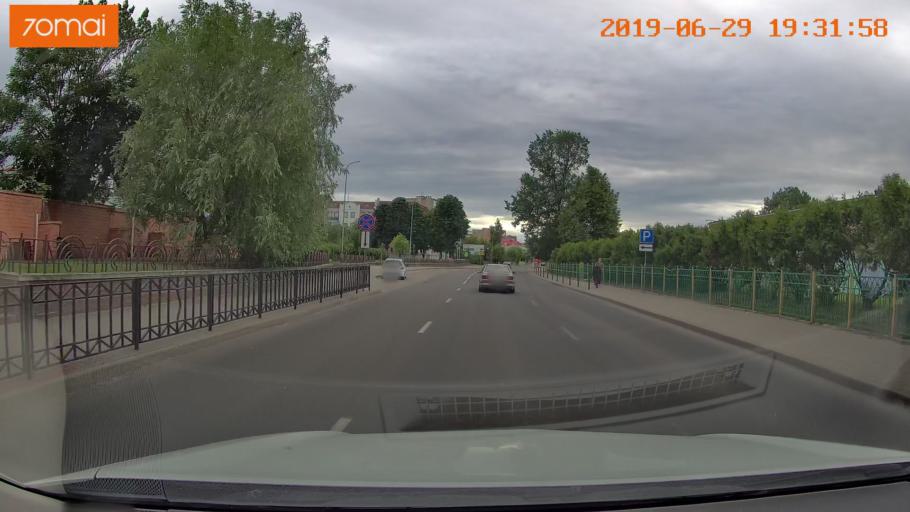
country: BY
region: Brest
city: Pinsk
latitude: 52.1160
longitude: 26.1077
